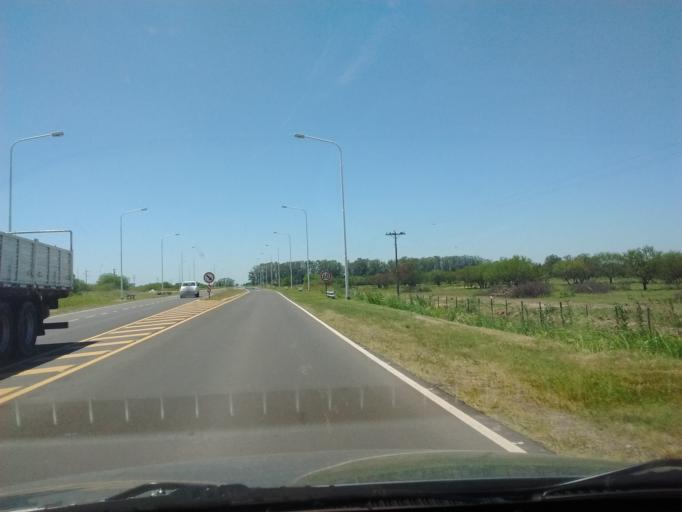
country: AR
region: Entre Rios
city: General Galarza
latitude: -32.8590
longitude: -59.7409
